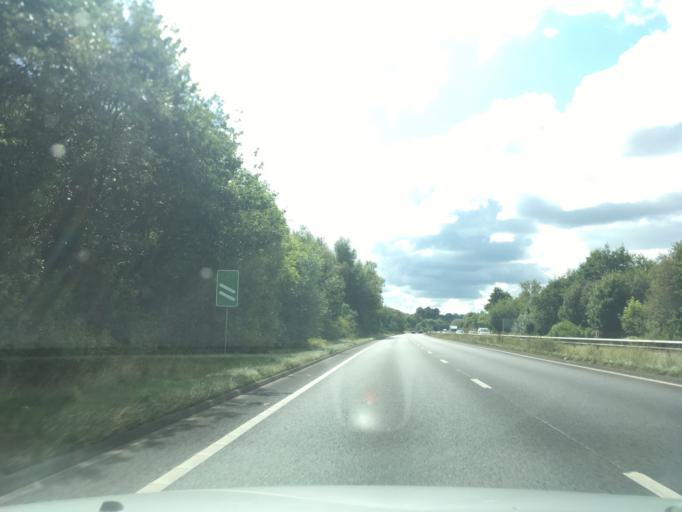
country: GB
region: England
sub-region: Hampshire
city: Liss
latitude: 51.0416
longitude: -0.9029
